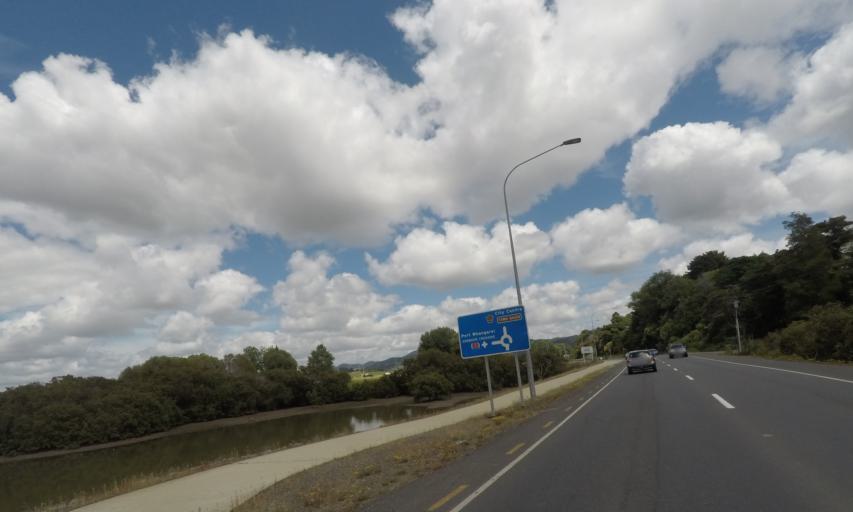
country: NZ
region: Northland
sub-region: Whangarei
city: Whangarei
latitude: -35.7318
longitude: 174.3449
